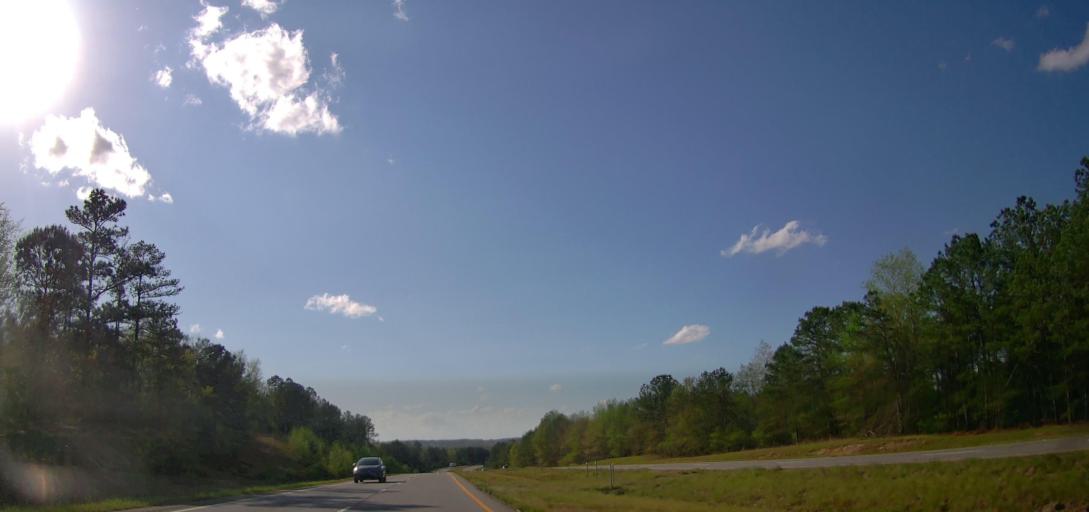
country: US
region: Georgia
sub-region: Baldwin County
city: Hardwick
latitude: 33.0248
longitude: -83.2387
